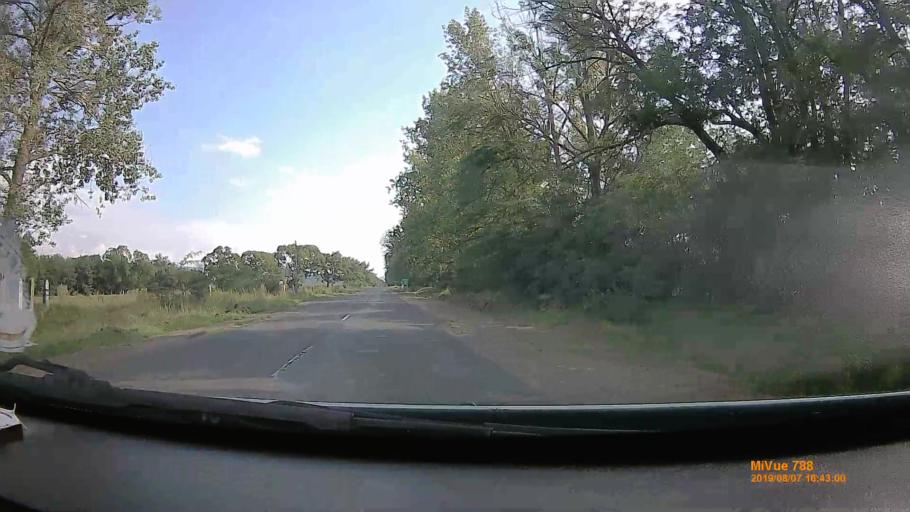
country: HU
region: Borsod-Abauj-Zemplen
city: Abaujszanto
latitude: 48.3632
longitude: 21.2157
